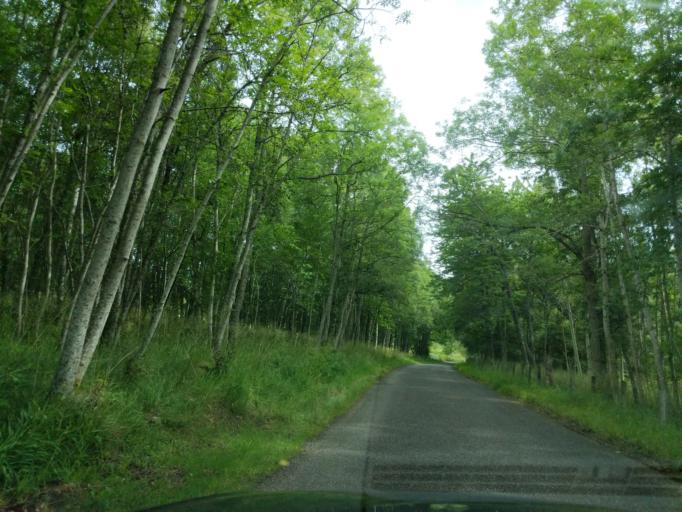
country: GB
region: Scotland
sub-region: Aberdeenshire
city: Aboyne
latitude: 57.0617
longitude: -2.8402
